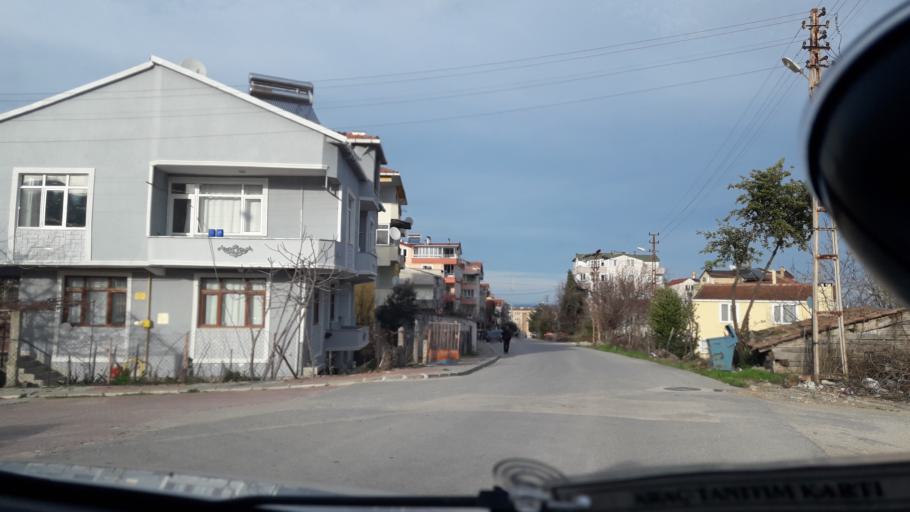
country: TR
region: Sinop
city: Gerze
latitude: 41.8048
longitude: 35.1845
